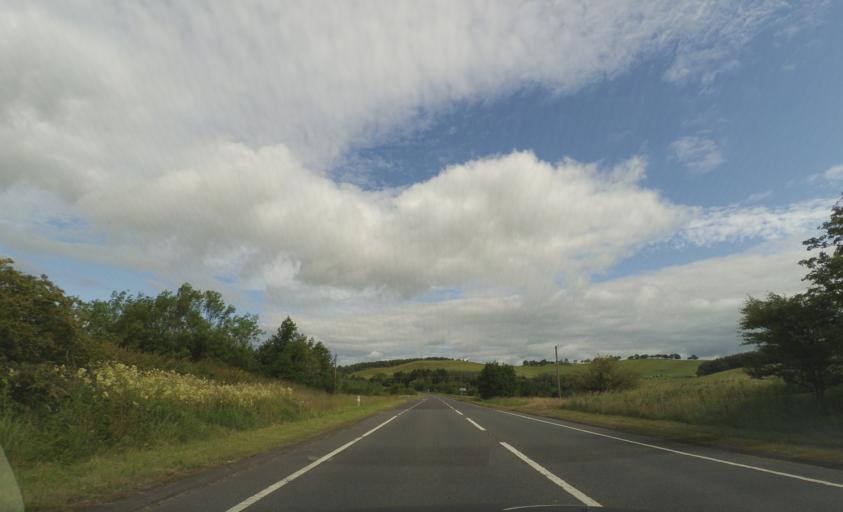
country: GB
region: Scotland
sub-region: The Scottish Borders
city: Selkirk
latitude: 55.5319
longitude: -2.8268
